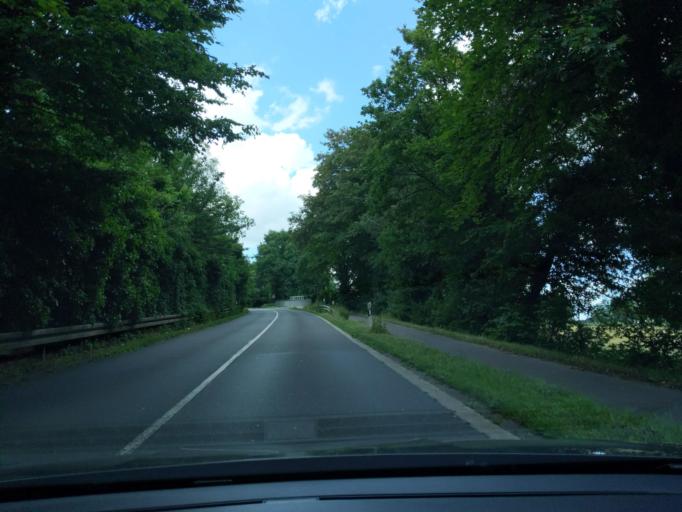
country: DE
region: North Rhine-Westphalia
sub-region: Regierungsbezirk Dusseldorf
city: Erkrath
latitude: 51.2284
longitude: 6.8968
